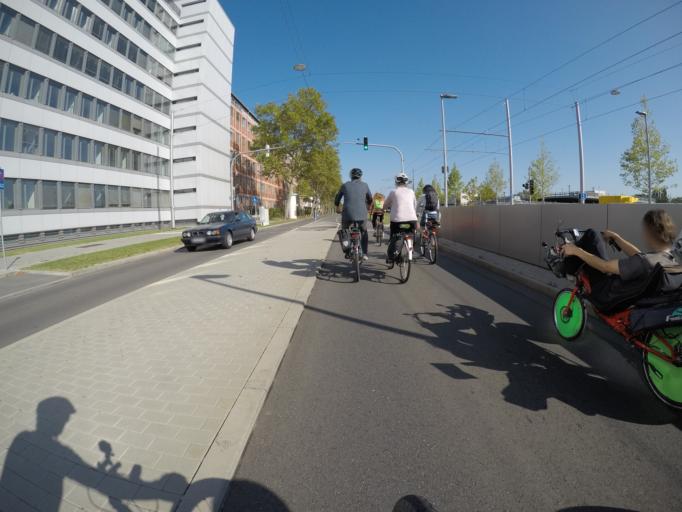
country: DE
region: Hesse
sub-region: Regierungsbezirk Darmstadt
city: Darmstadt
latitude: 49.8959
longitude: 8.6542
